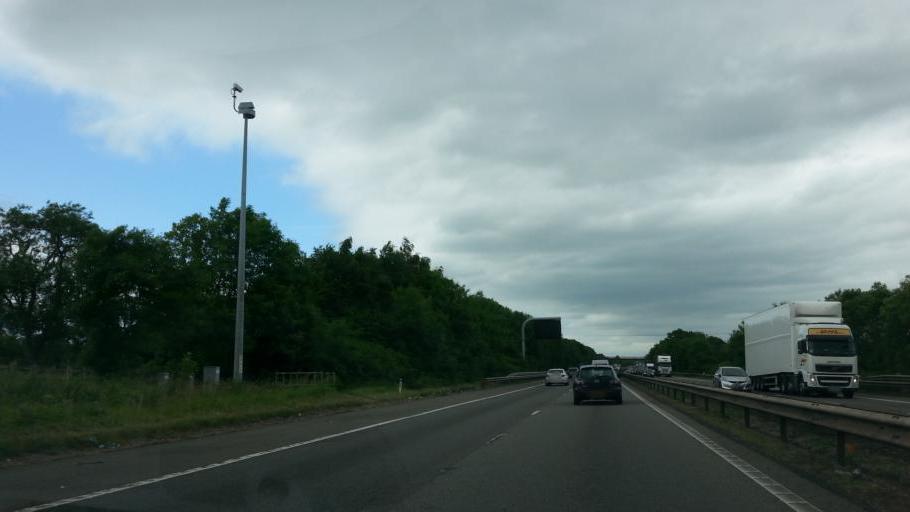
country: GB
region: England
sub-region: Derbyshire
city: Netherseal
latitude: 52.6575
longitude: -1.5822
